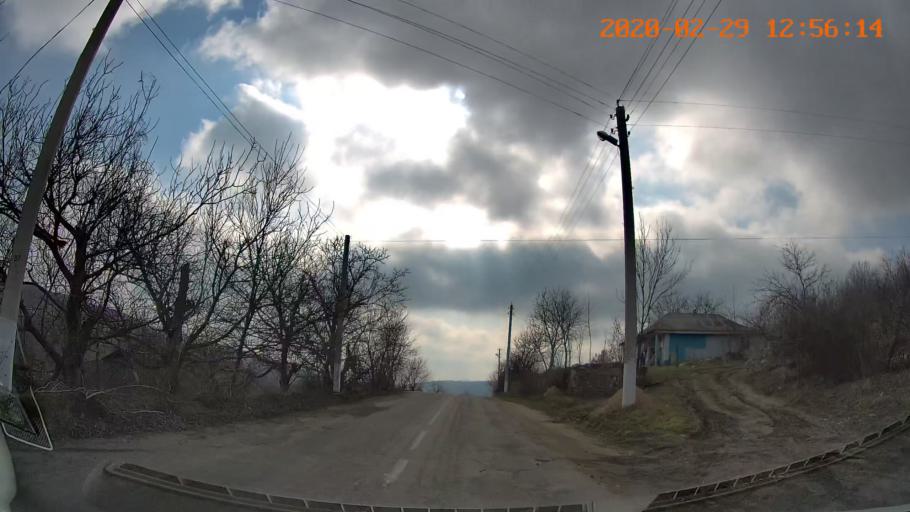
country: MD
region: Telenesti
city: Camenca
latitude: 48.0887
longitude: 28.7229
